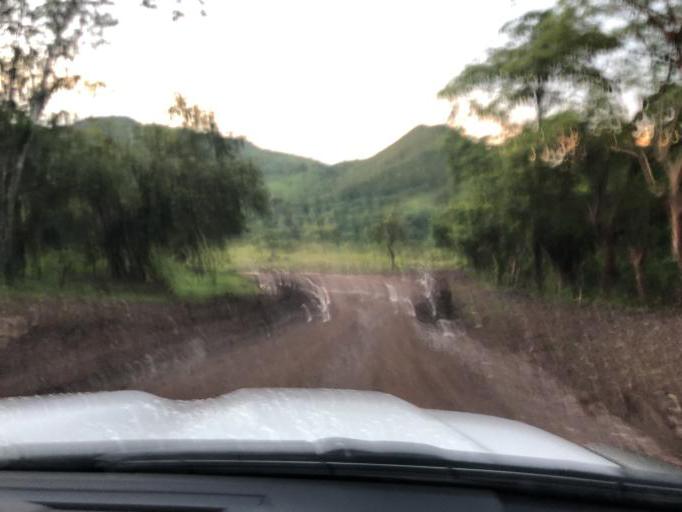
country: NI
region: Chontales
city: La Libertad
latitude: 12.1812
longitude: -85.1716
